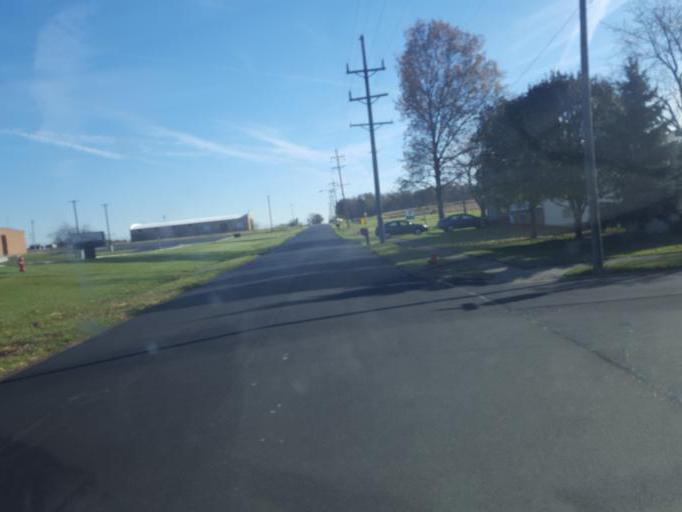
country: US
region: Ohio
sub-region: Crawford County
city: Bucyrus
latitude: 40.7979
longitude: -82.9555
